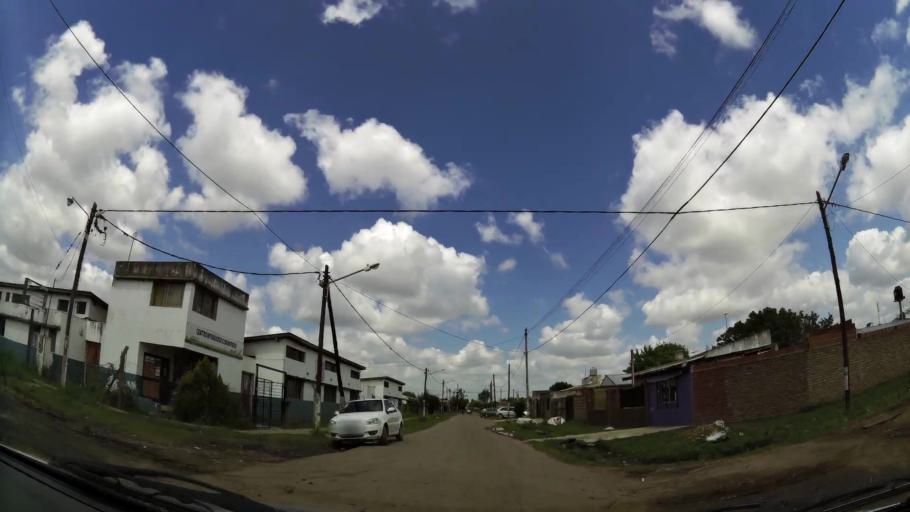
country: AR
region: Buenos Aires
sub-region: Partido de Quilmes
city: Quilmes
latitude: -34.8328
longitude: -58.2277
